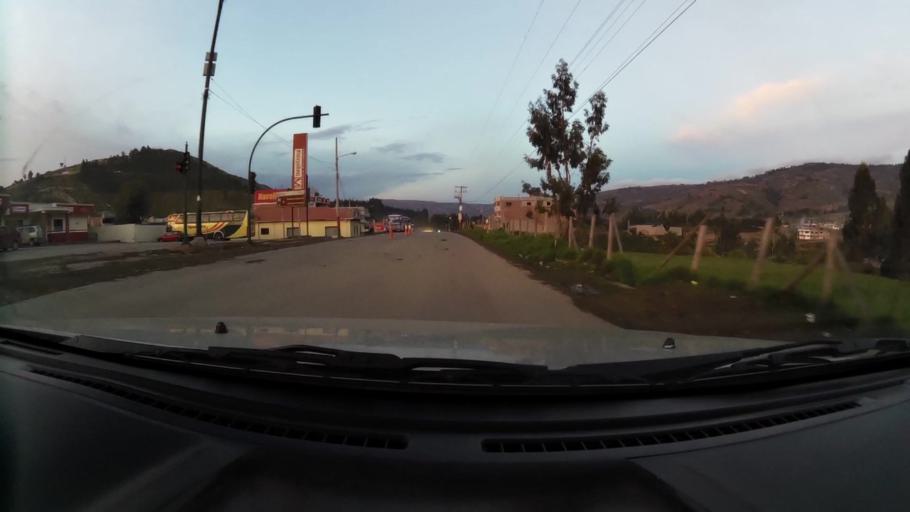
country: EC
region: Chimborazo
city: Riobamba
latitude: -1.9347
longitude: -78.7070
